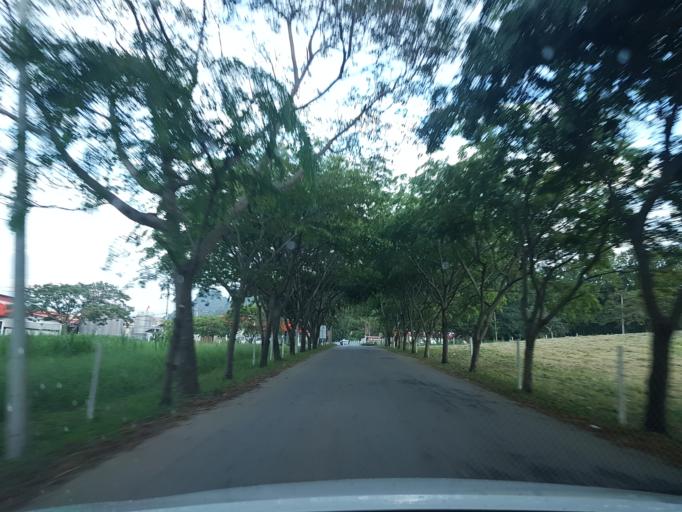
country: TH
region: Sara Buri
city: Muak Lek
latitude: 14.6307
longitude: 101.1996
